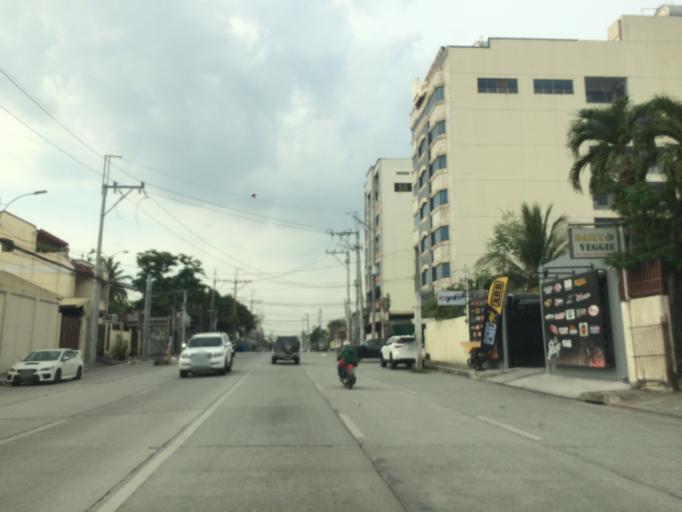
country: PH
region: Calabarzon
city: Del Monte
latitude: 14.6367
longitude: 121.0058
